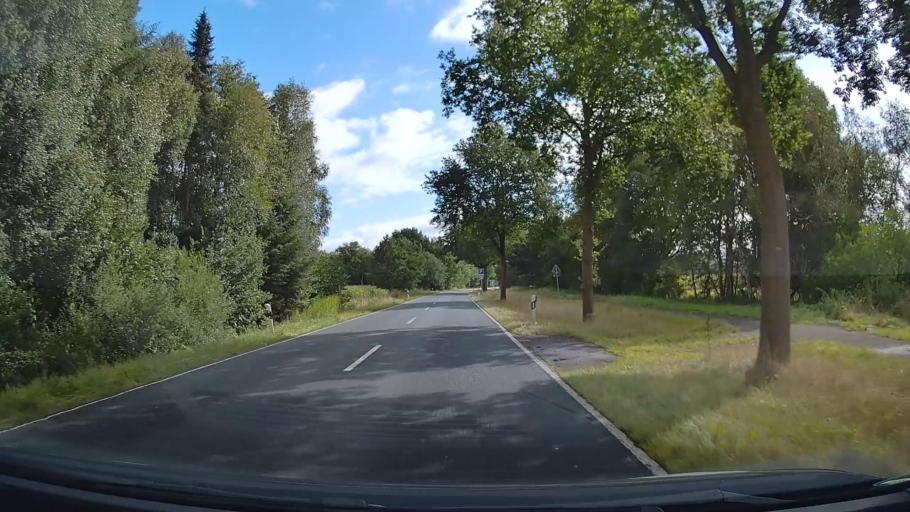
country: DE
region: Lower Saxony
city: Rhade
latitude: 53.3386
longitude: 9.1023
